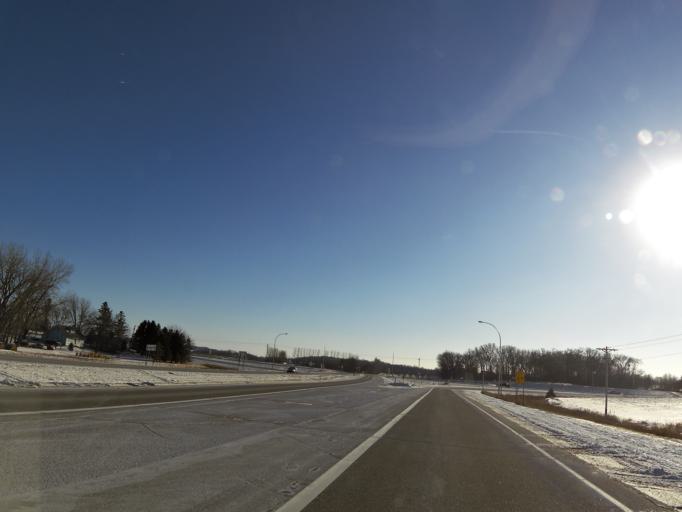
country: US
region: Minnesota
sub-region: Le Sueur County
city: New Prague
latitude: 44.5458
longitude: -93.5021
